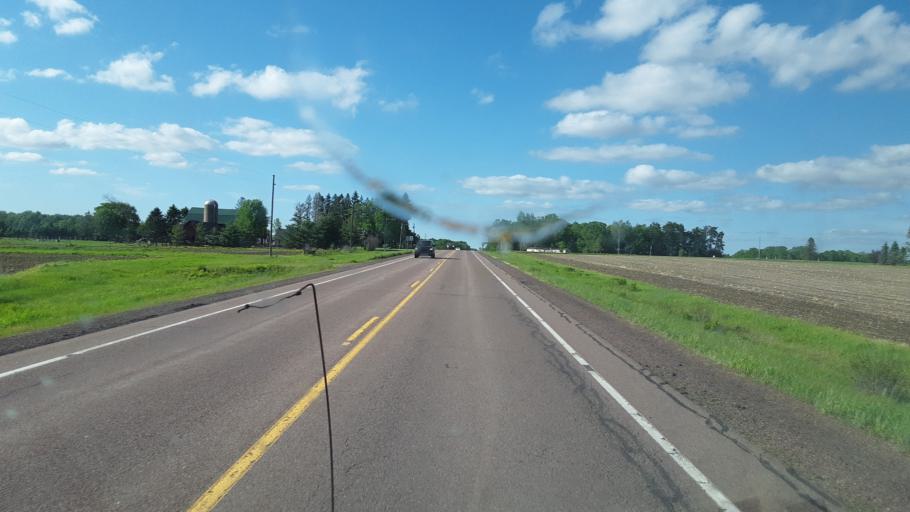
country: US
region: Wisconsin
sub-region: Wood County
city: Marshfield
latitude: 44.5812
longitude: -90.1808
